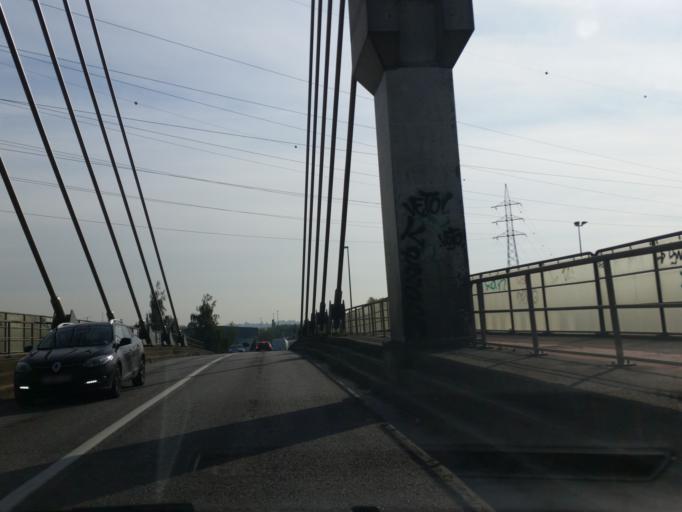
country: BE
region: Flanders
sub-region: Provincie Vlaams-Brabant
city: Drogenbos
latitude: 50.8020
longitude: 4.3032
